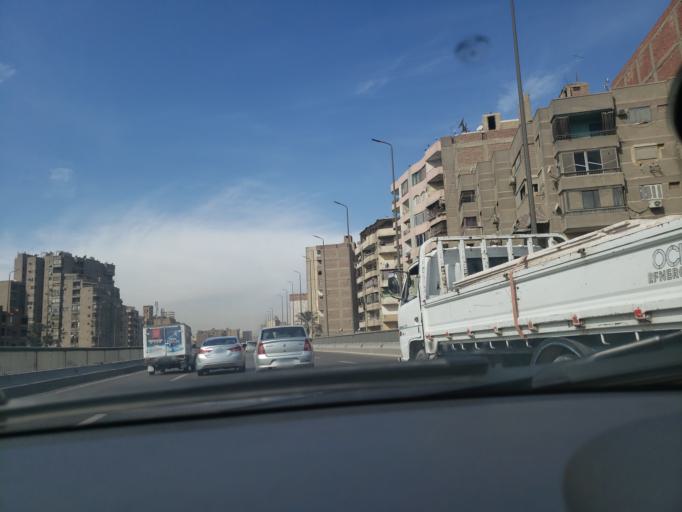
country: EG
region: Al Jizah
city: Al Jizah
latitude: 29.9817
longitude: 31.1571
